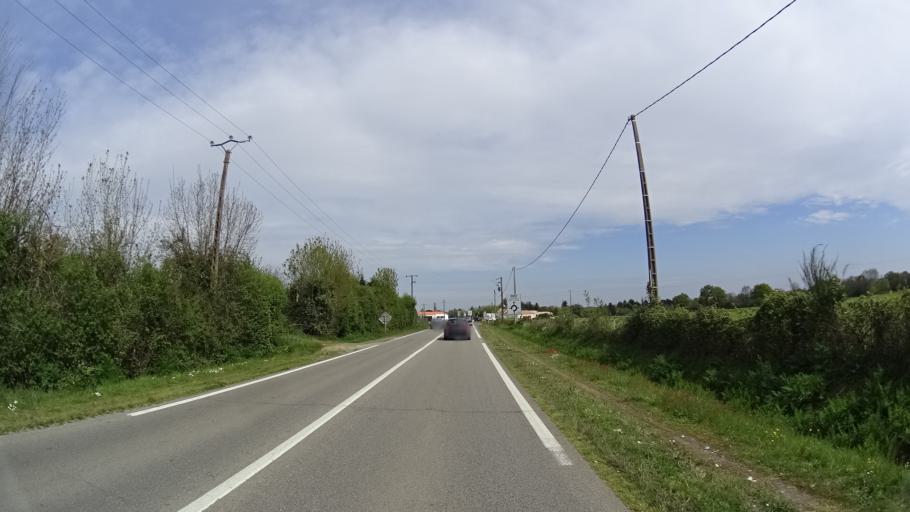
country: FR
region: Pays de la Loire
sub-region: Departement de la Loire-Atlantique
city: Port-Saint-Pere
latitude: 47.1287
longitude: -1.7600
